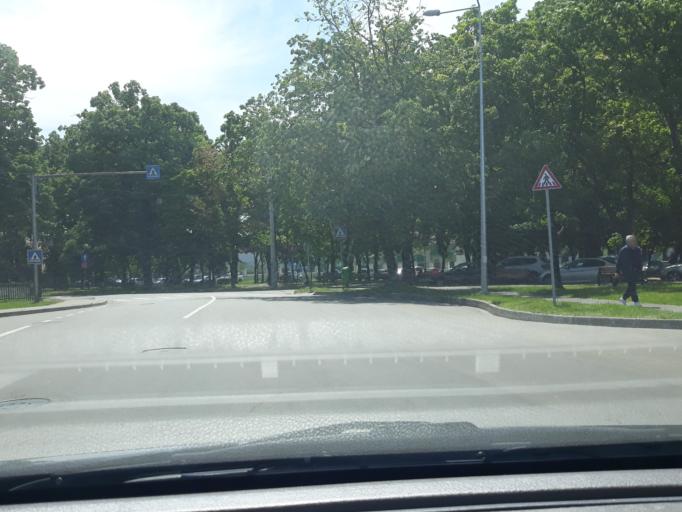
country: RO
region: Bihor
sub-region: Comuna Biharea
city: Oradea
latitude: 47.0511
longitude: 21.9197
